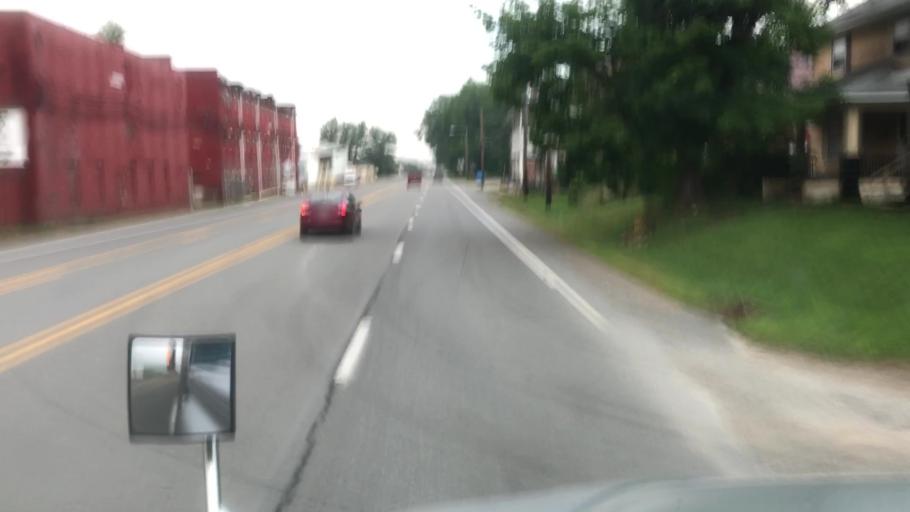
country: US
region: Pennsylvania
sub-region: Venango County
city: Woodland Heights
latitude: 41.4089
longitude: -79.7512
